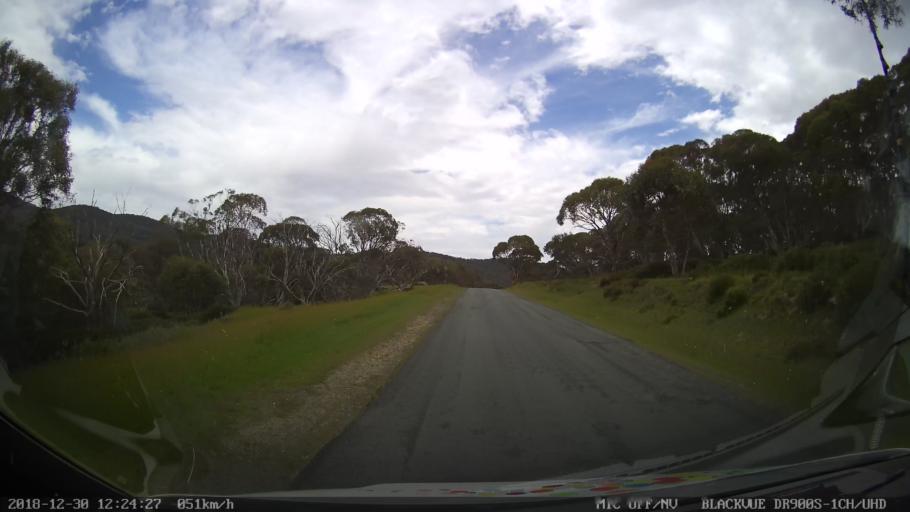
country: AU
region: New South Wales
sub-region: Snowy River
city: Jindabyne
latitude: -36.3562
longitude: 148.4919
